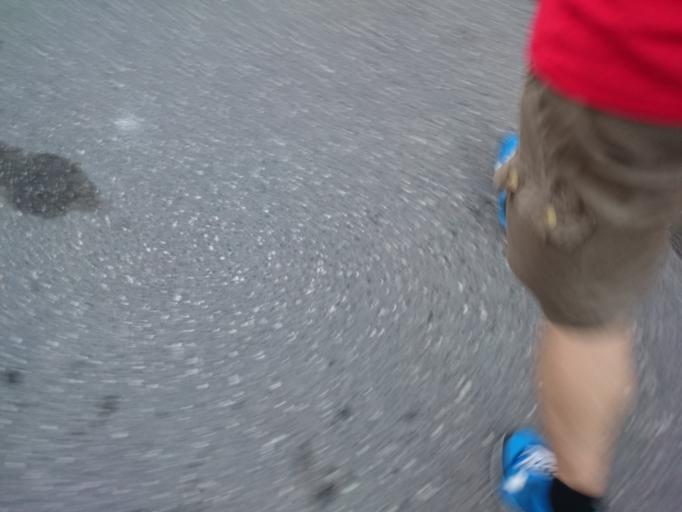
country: AL
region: Shkoder
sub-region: Rrethi i Shkodres
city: Shkoder
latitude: 42.0640
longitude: 19.5198
